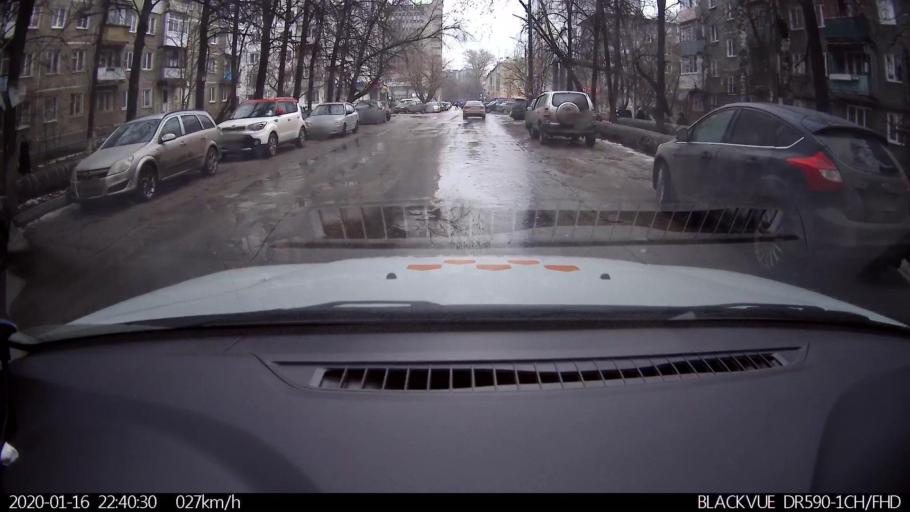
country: RU
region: Nizjnij Novgorod
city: Nizhniy Novgorod
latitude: 56.2770
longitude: 43.9189
